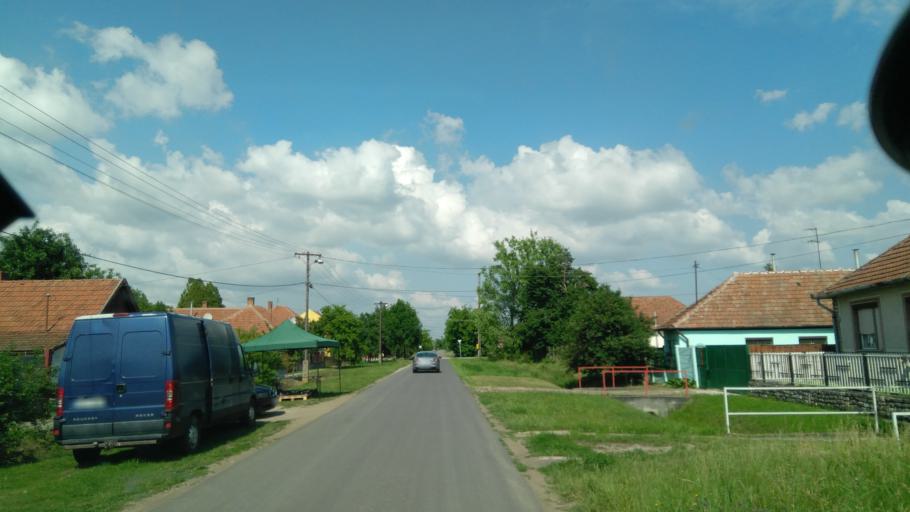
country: HU
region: Bekes
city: Doboz
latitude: 46.7388
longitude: 21.2348
